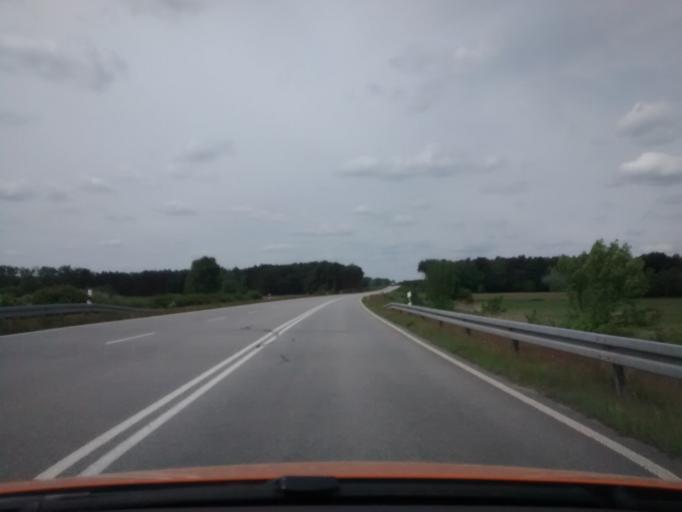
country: DE
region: Brandenburg
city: Luckenwalde
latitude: 52.1233
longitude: 13.1994
